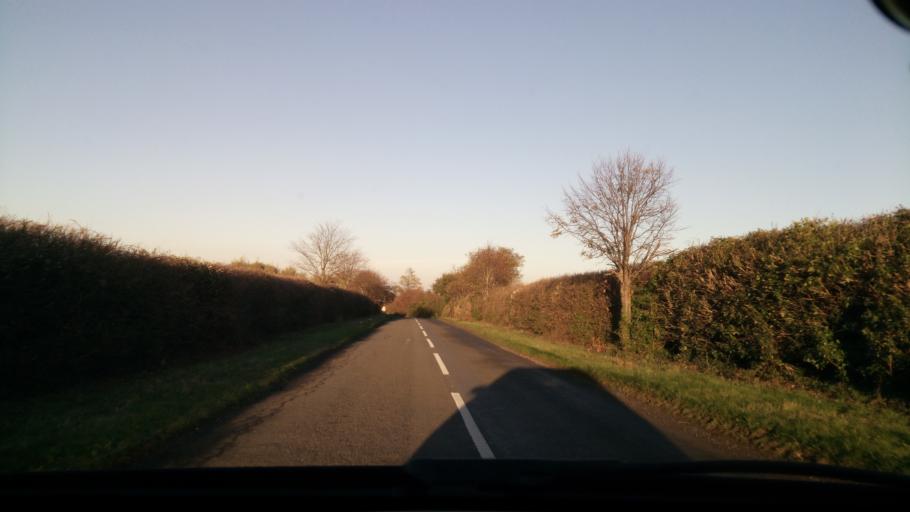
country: GB
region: England
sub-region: Peterborough
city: Barnack
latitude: 52.6288
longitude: -0.4177
